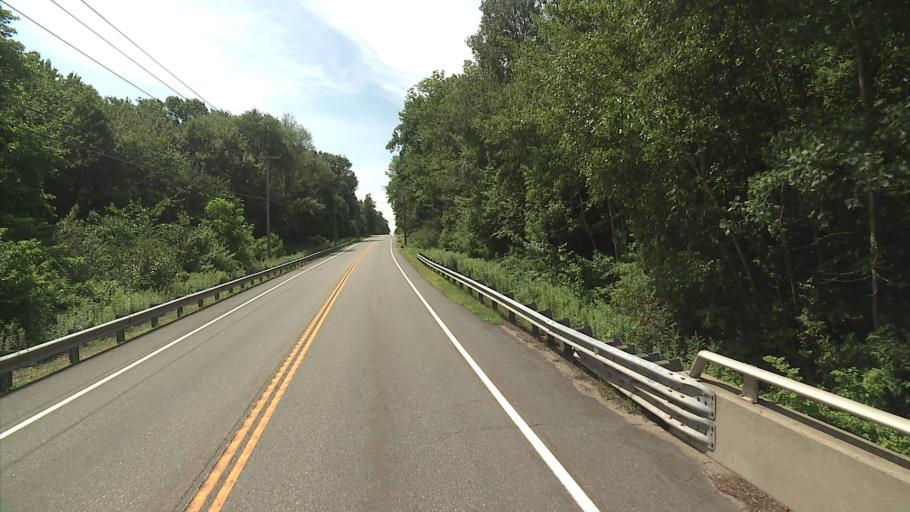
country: US
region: Connecticut
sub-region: Tolland County
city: Tolland
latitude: 41.8247
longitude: -72.3984
